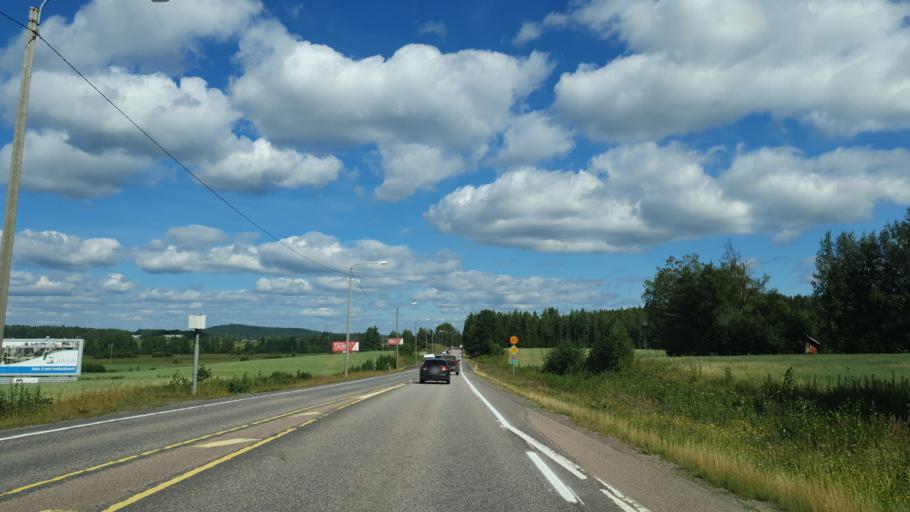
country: FI
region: Central Finland
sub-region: Jaemsae
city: Jaemsae
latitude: 61.8469
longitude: 25.1508
